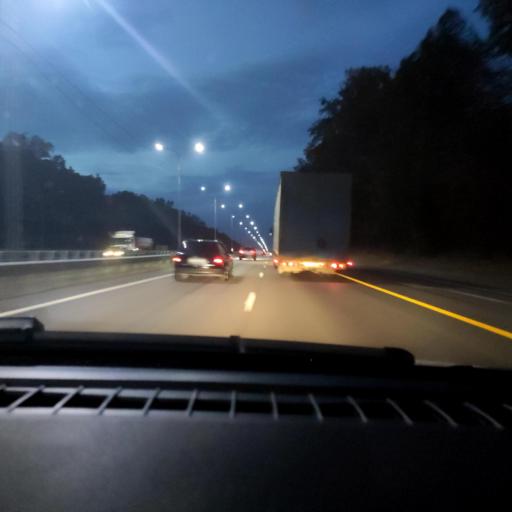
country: RU
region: Voronezj
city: Ramon'
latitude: 51.8561
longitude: 39.2154
